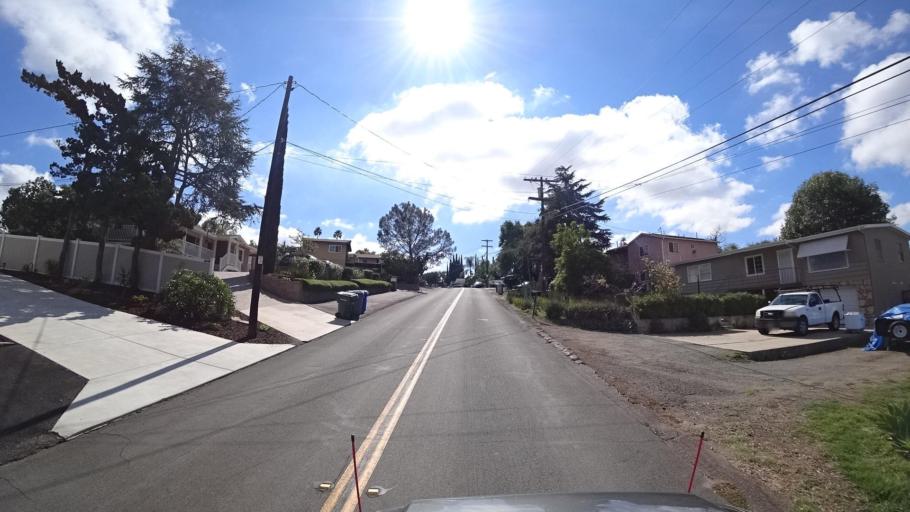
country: US
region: California
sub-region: San Diego County
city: Casa de Oro-Mount Helix
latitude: 32.7408
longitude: -116.9655
